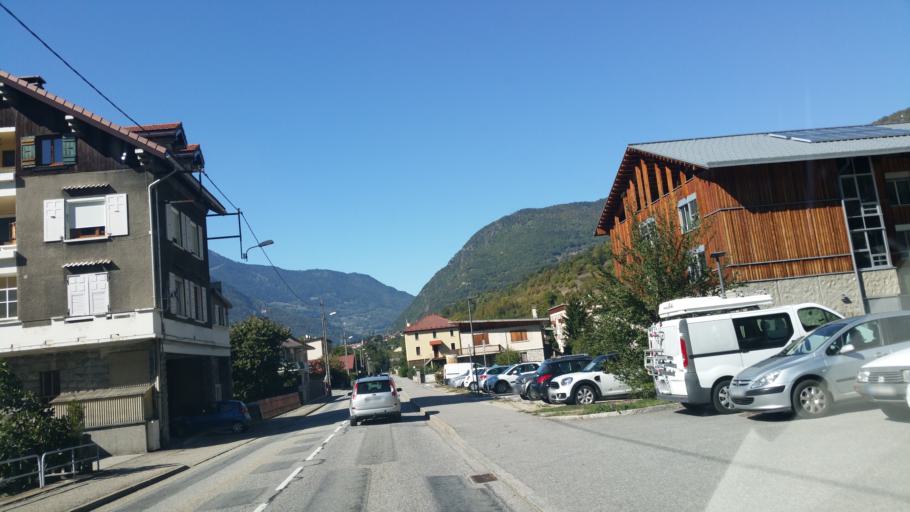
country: FR
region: Rhone-Alpes
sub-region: Departement de la Savoie
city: Aigueblanche
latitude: 45.5040
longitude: 6.5065
